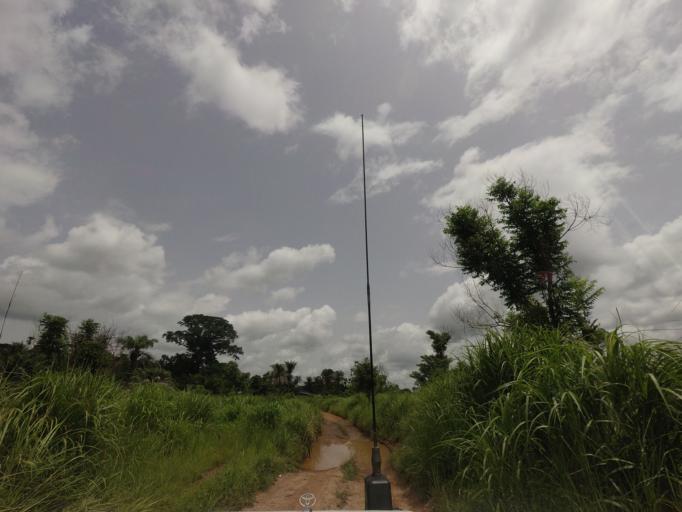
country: SL
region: Eastern Province
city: Buedu
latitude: 8.4870
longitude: -10.3337
